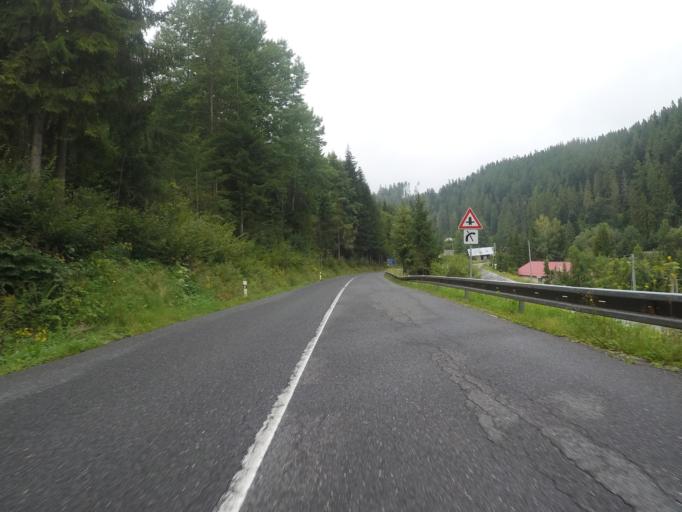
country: SK
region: Kosicky
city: Spisska Nova Ves
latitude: 48.8747
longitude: 20.5247
